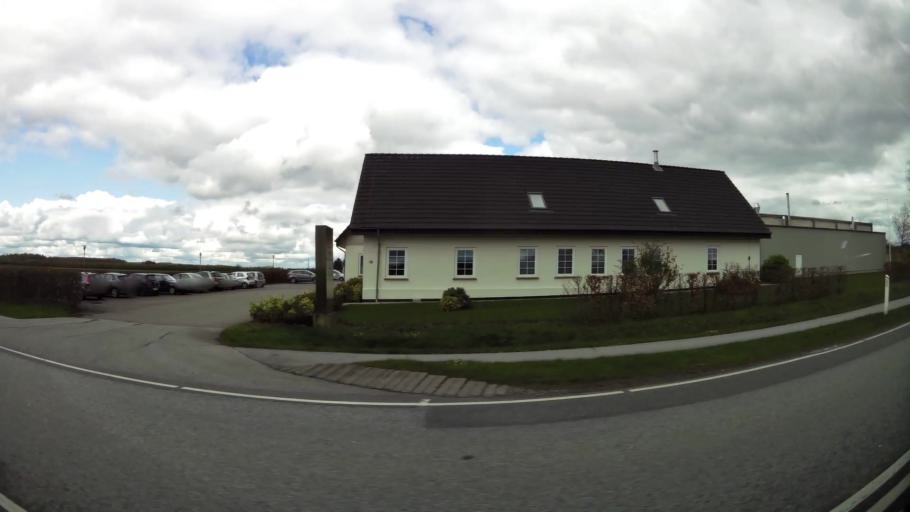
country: DK
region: South Denmark
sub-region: Haderslev Kommune
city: Vojens
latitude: 55.2438
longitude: 9.2788
